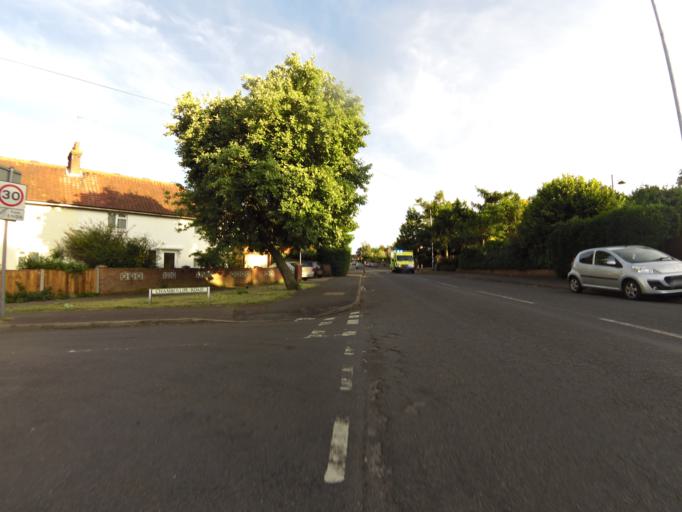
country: GB
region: England
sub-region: Norfolk
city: Norwich
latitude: 52.6463
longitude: 1.2911
